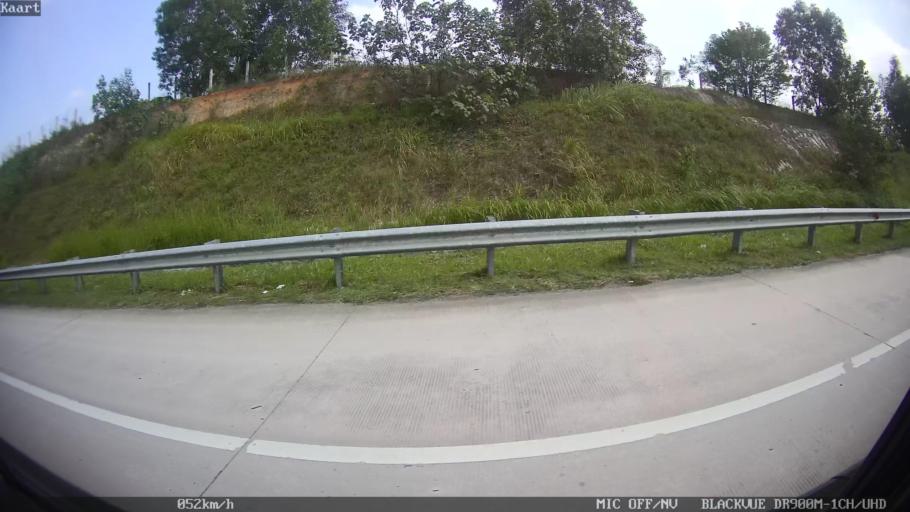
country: ID
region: Lampung
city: Natar
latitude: -5.2818
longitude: 105.2048
